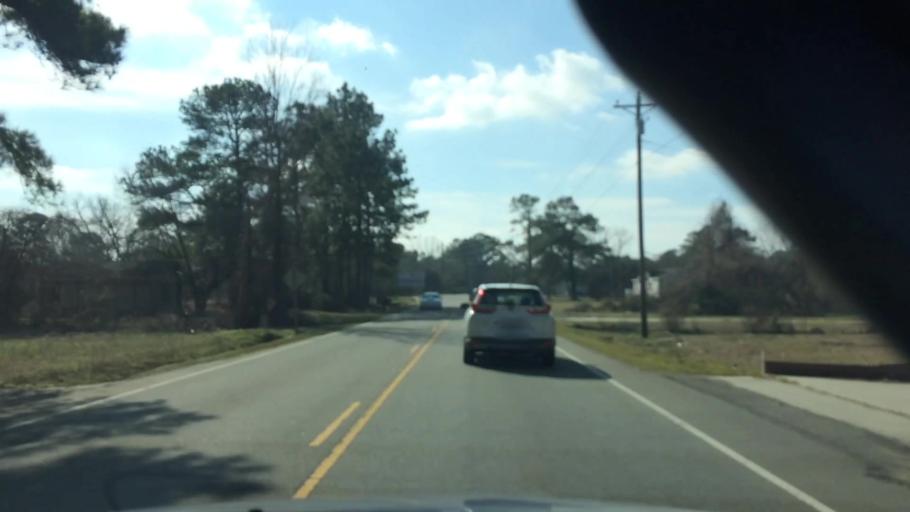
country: US
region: North Carolina
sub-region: Duplin County
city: Wallace
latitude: 34.7779
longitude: -77.9136
